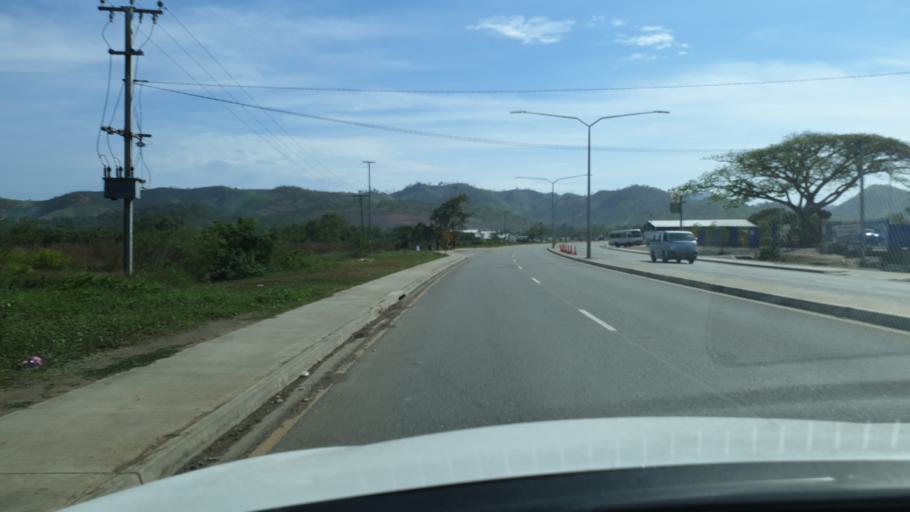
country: PG
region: National Capital
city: Port Moresby
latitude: -9.4779
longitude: 147.2434
